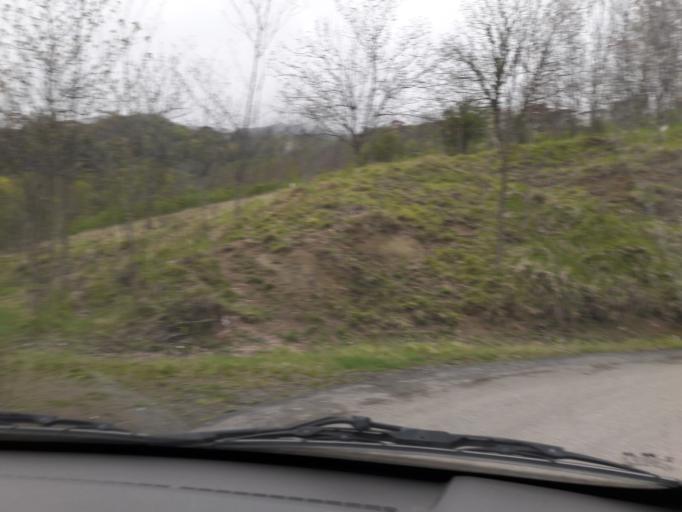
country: TR
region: Trabzon
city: Duzkoy
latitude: 40.9302
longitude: 39.4780
